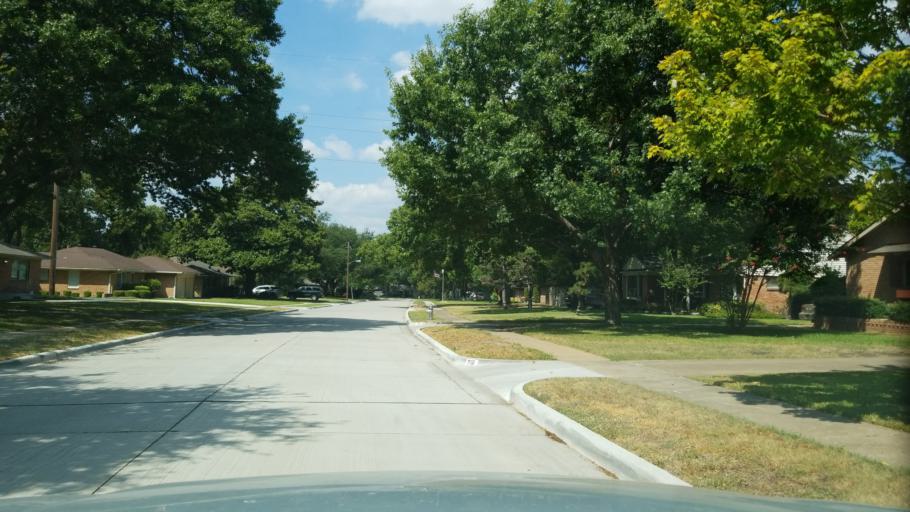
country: US
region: Texas
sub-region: Dallas County
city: Richardson
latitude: 32.9556
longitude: -96.7452
